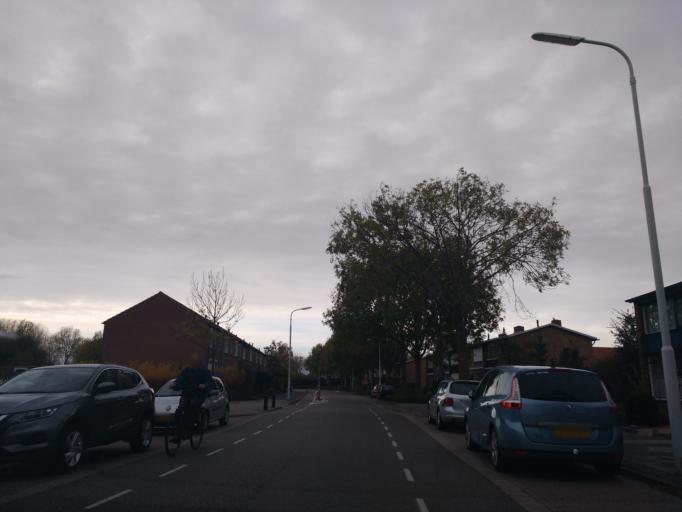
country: NL
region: Zeeland
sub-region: Gemeente Vlissingen
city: Vlissingen
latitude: 51.3968
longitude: 3.5511
